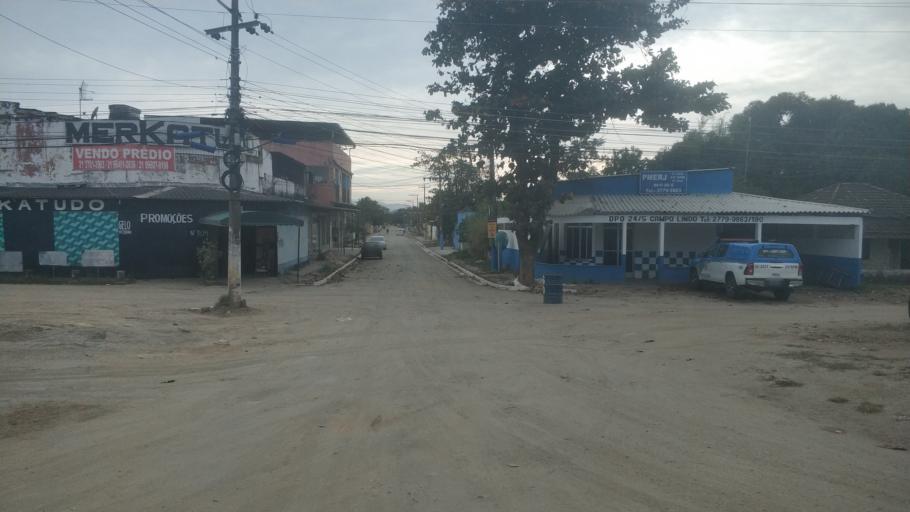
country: BR
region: Rio de Janeiro
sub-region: Seropedica
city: Seropedica
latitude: -22.8009
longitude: -43.6435
